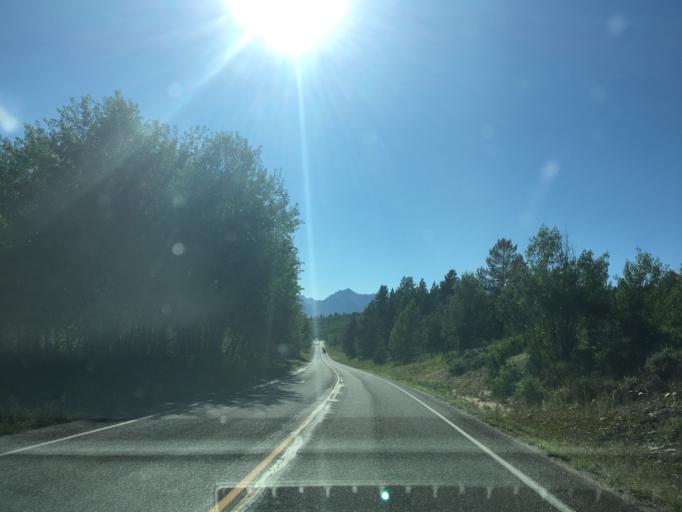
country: US
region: Wyoming
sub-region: Teton County
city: Jackson
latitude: 43.8655
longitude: -110.5407
